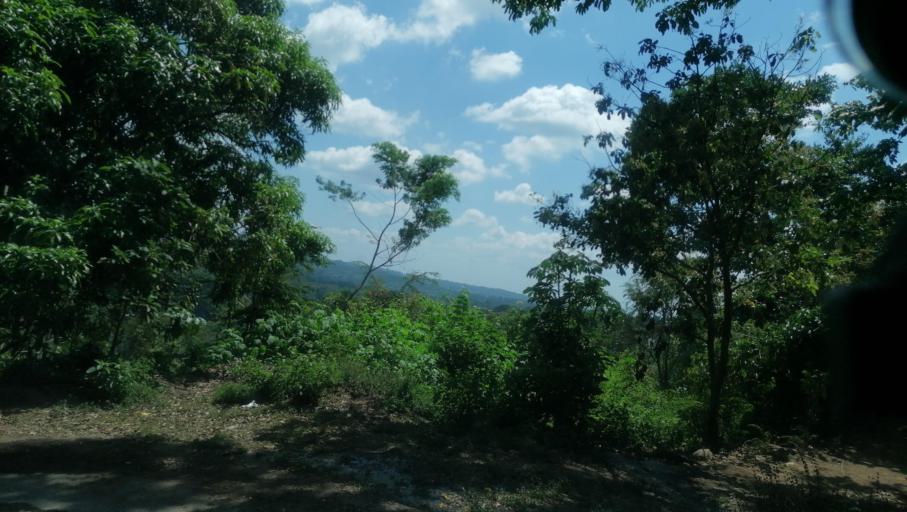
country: MX
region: Chiapas
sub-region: Union Juarez
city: Santo Domingo
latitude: 15.0368
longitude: -92.1434
